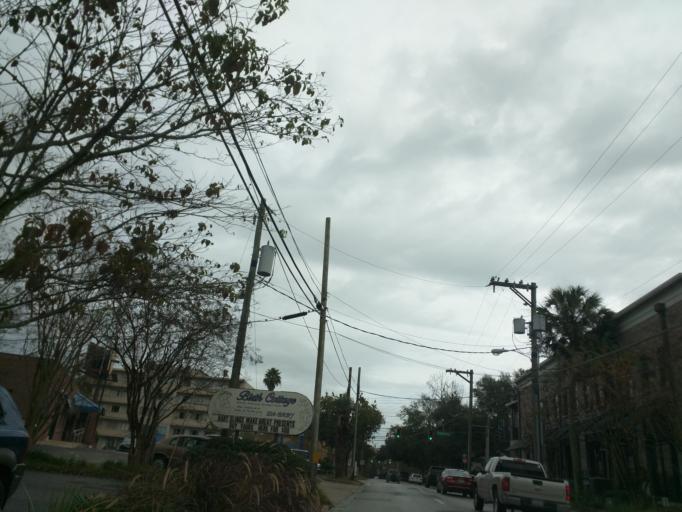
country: US
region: Florida
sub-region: Leon County
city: Tallahassee
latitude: 30.4563
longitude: -84.2783
